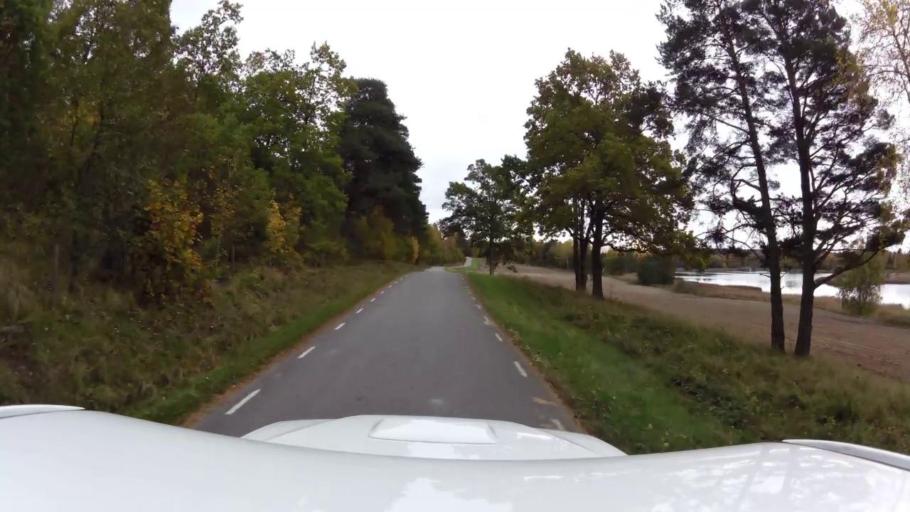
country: SE
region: OEstergoetland
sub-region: Linkopings Kommun
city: Ljungsbro
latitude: 58.5278
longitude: 15.4635
